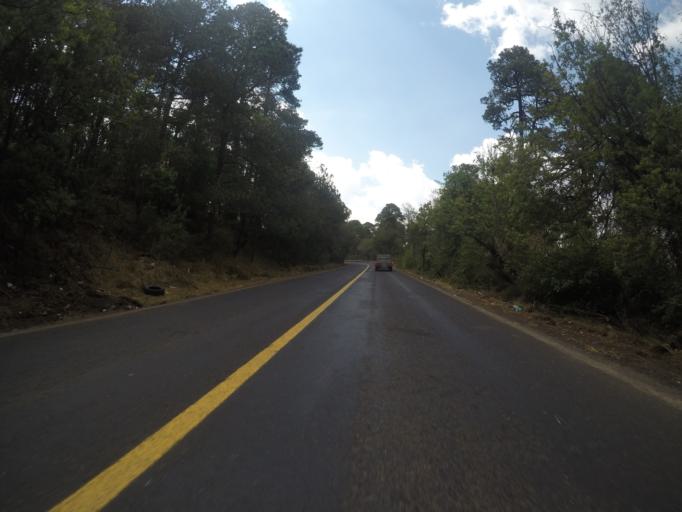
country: MX
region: Mexico
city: Cerro La Calera
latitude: 19.1355
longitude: -99.8137
